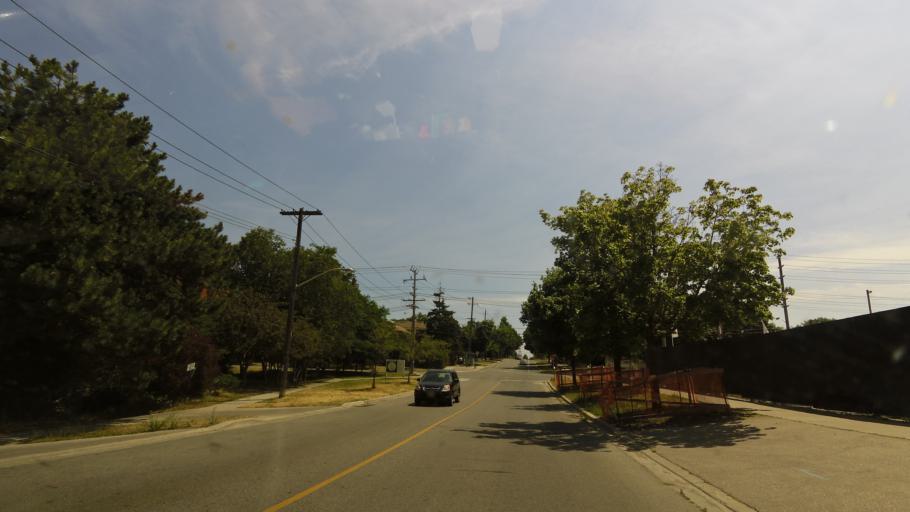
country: CA
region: Ontario
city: Etobicoke
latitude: 43.6381
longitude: -79.4875
